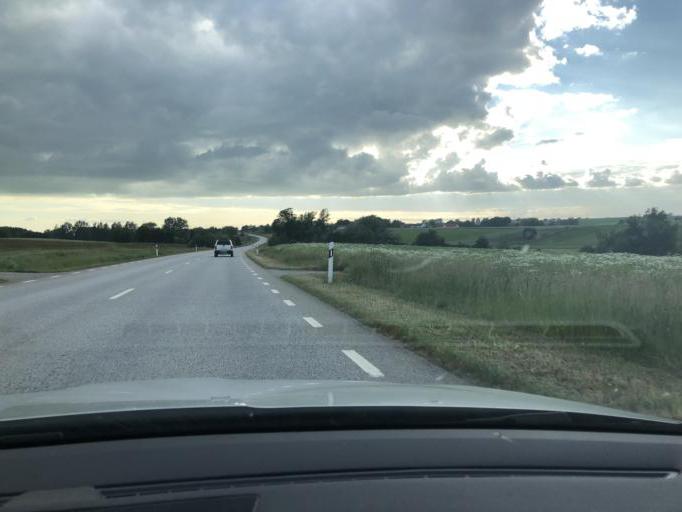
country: SE
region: Skane
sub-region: Simrishamns Kommun
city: Simrishamn
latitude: 55.5354
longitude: 14.3025
